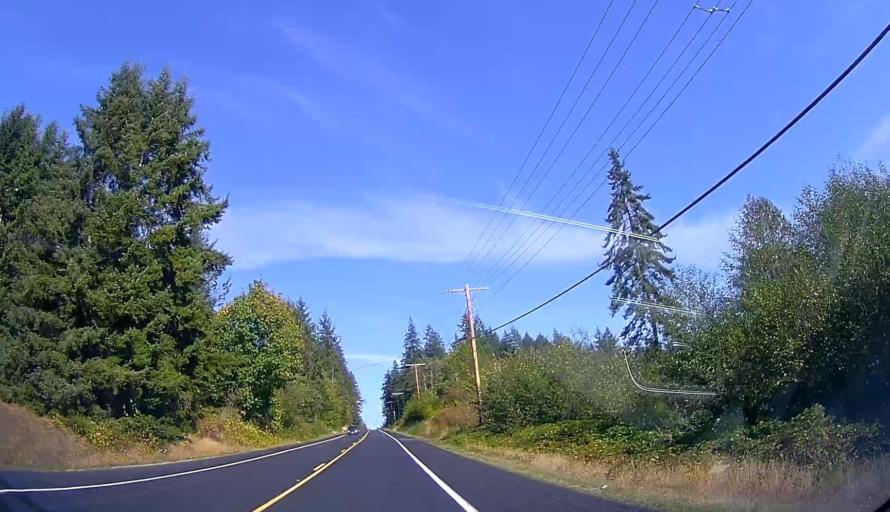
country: US
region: Washington
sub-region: Island County
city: Camano
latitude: 48.1850
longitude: -122.5134
